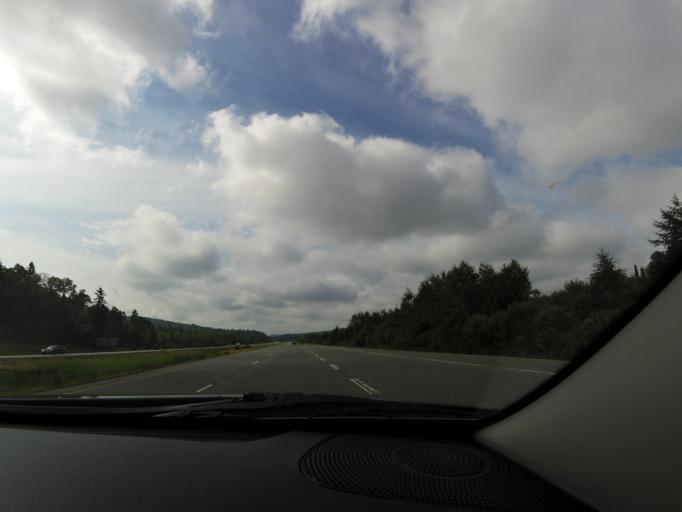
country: CA
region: Ontario
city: Huntsville
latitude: 45.4067
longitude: -79.2399
